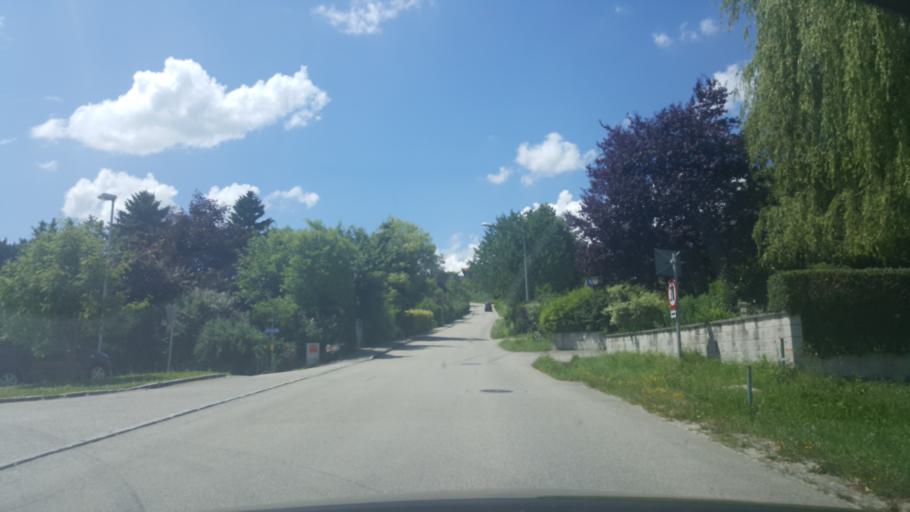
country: AT
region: Upper Austria
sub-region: Politischer Bezirk Vocklabruck
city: Seewalchen
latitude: 47.9557
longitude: 13.5835
